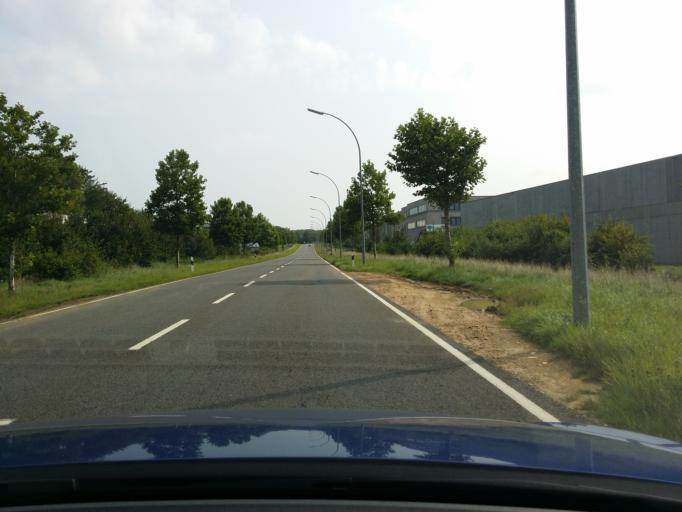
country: LU
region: Luxembourg
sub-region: Canton de Luxembourg
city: Strassen
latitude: 49.6103
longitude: 6.0742
